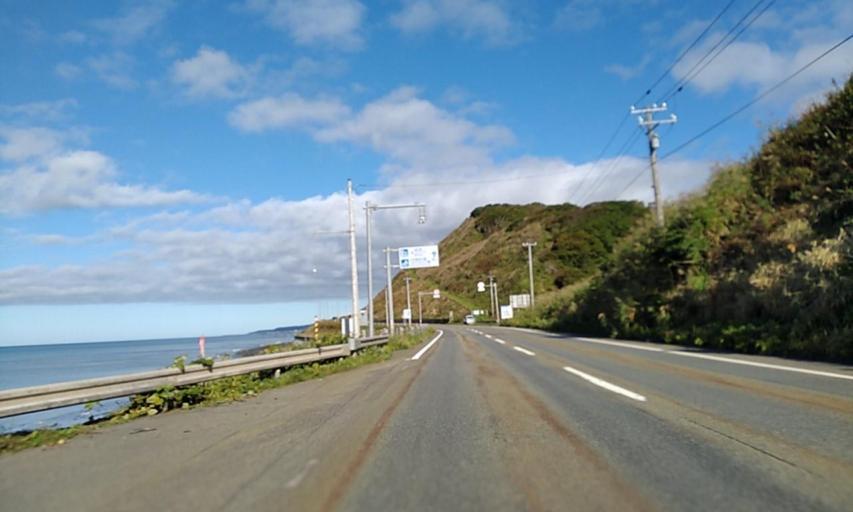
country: JP
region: Hokkaido
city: Shizunai-furukawacho
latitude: 42.2083
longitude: 142.6500
